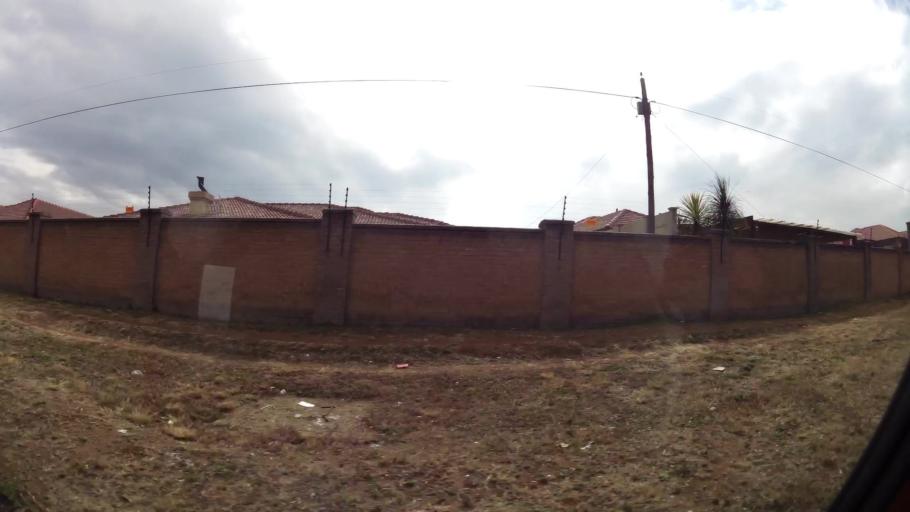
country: ZA
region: Gauteng
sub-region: Sedibeng District Municipality
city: Vanderbijlpark
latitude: -26.7286
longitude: 27.8696
